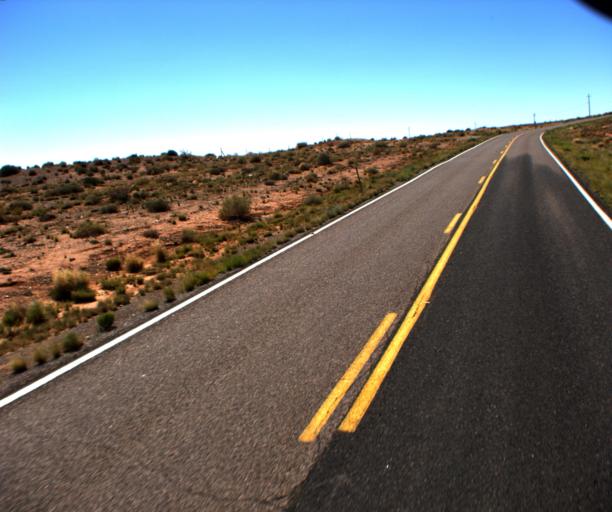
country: US
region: Arizona
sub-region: Coconino County
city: LeChee
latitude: 35.1270
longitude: -110.8752
